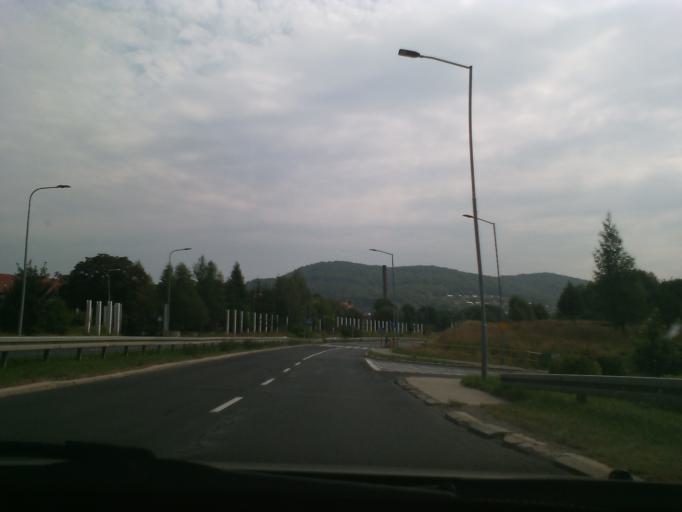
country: PL
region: Lower Silesian Voivodeship
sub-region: Powiat walbrzyski
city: Walbrzych
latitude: 50.7573
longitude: 16.2801
